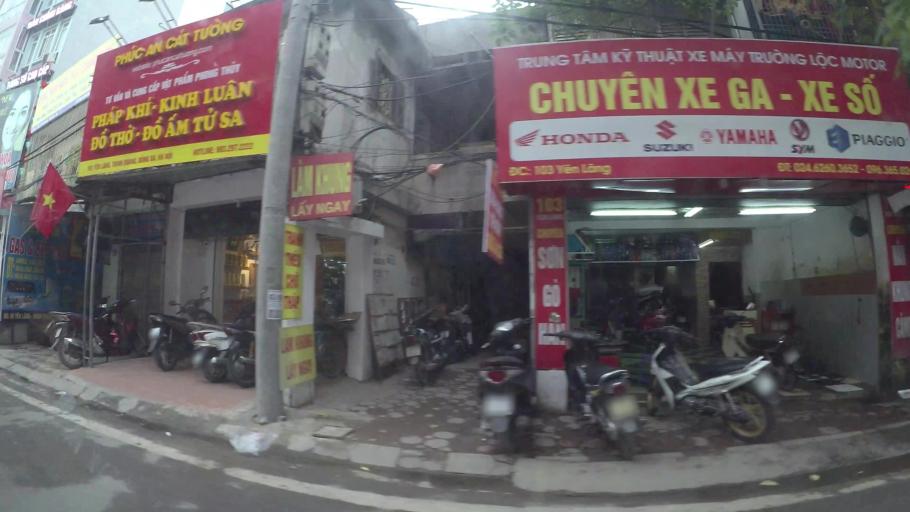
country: VN
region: Ha Noi
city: Dong Da
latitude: 21.0108
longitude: 105.8165
